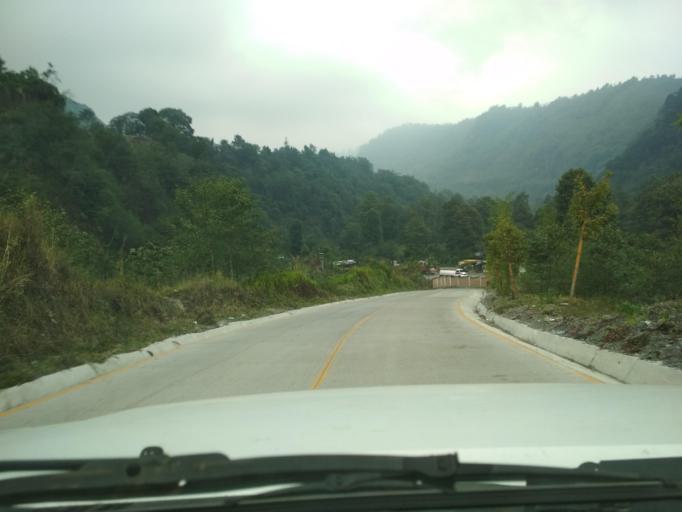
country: MX
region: Veracruz
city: La Perla
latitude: 18.9298
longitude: -97.1383
